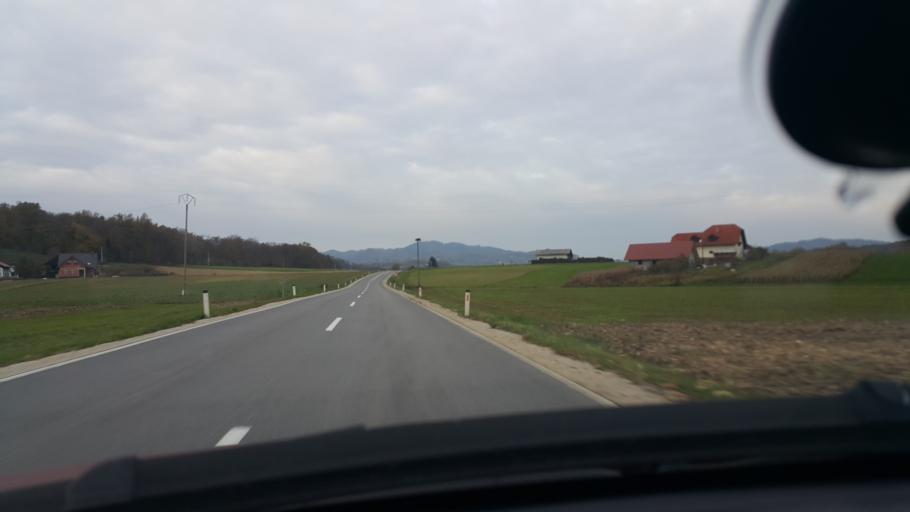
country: SI
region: Kozje
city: Kozje
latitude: 46.0972
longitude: 15.6131
